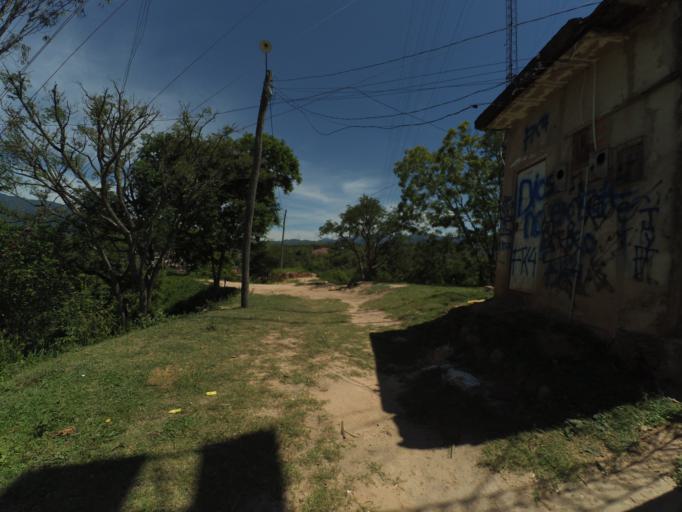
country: BO
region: Chuquisaca
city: Monteagudo
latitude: -19.8026
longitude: -63.9529
